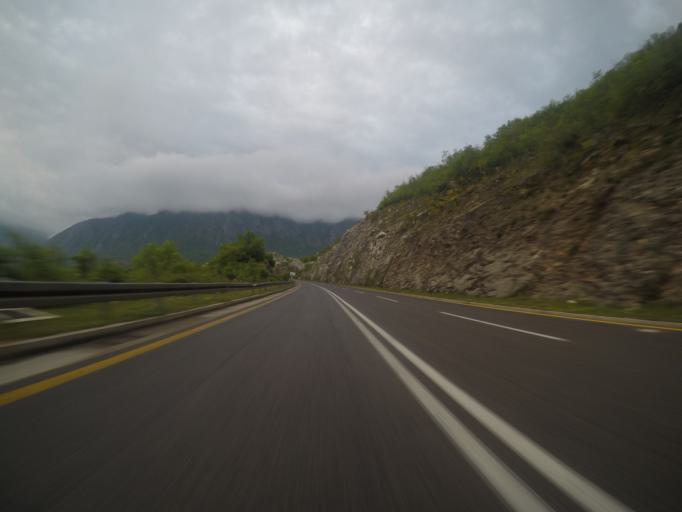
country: ME
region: Bar
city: Sutomore
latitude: 42.2120
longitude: 19.0480
